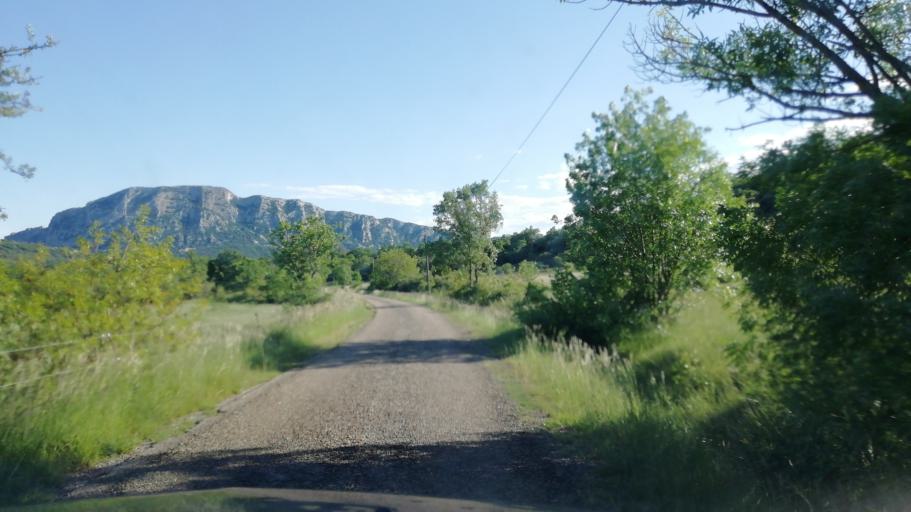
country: FR
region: Languedoc-Roussillon
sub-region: Departement de l'Herault
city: Saint-Mathieu-de-Treviers
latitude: 43.8060
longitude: 3.8098
